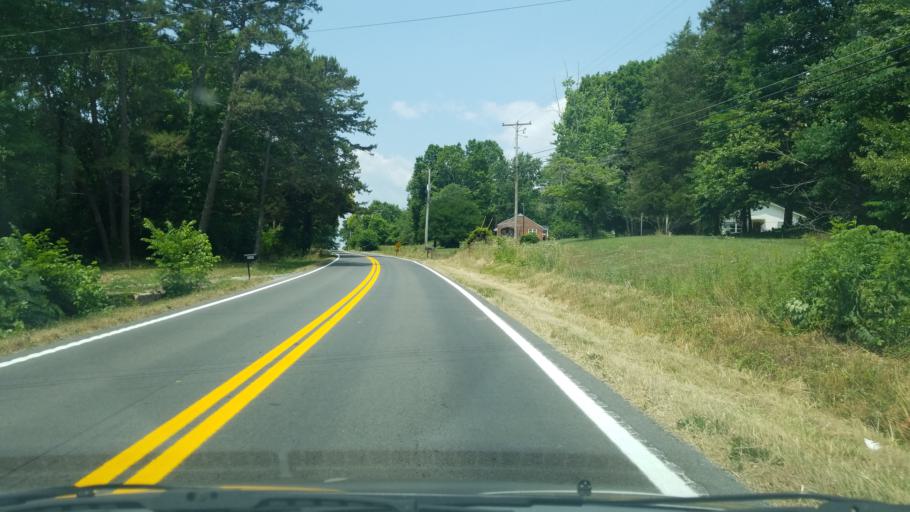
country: US
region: Tennessee
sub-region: Hamilton County
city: Lakesite
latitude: 35.2049
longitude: -85.1435
